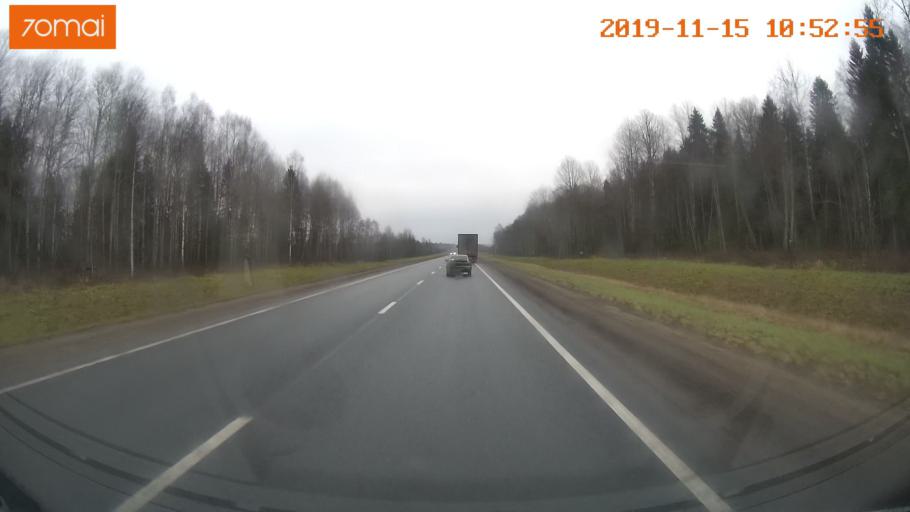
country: RU
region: Vologda
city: Chebsara
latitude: 59.1717
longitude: 38.7429
